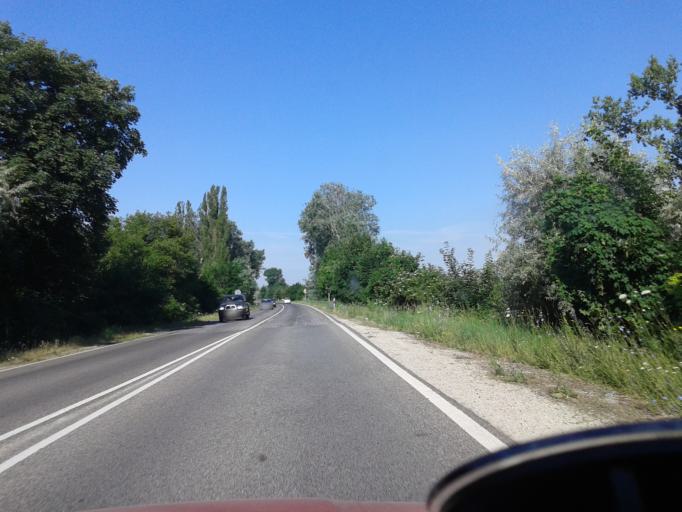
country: HU
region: Pest
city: Biatorbagy
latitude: 47.4911
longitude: 18.8123
